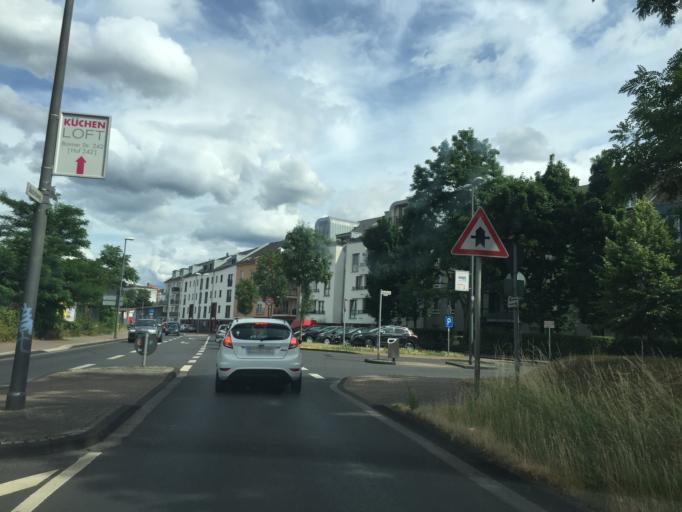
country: DE
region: North Rhine-Westphalia
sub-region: Regierungsbezirk Koln
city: Bayenthal
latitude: 50.9111
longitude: 6.9551
